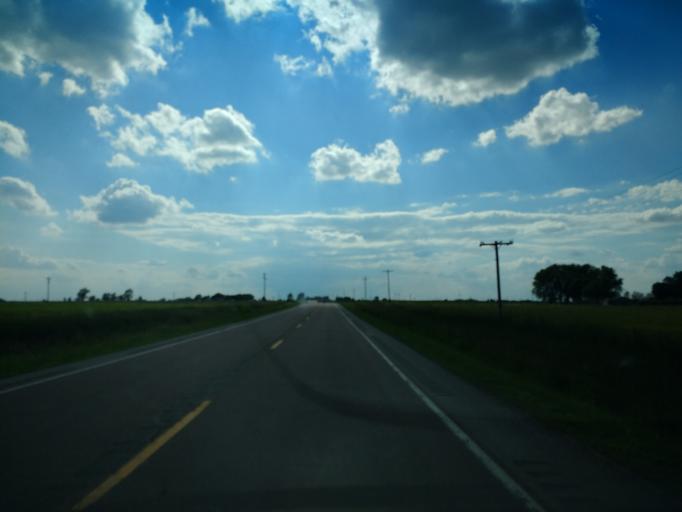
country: US
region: Iowa
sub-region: Clay County
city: Spencer
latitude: 43.1838
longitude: -95.2278
